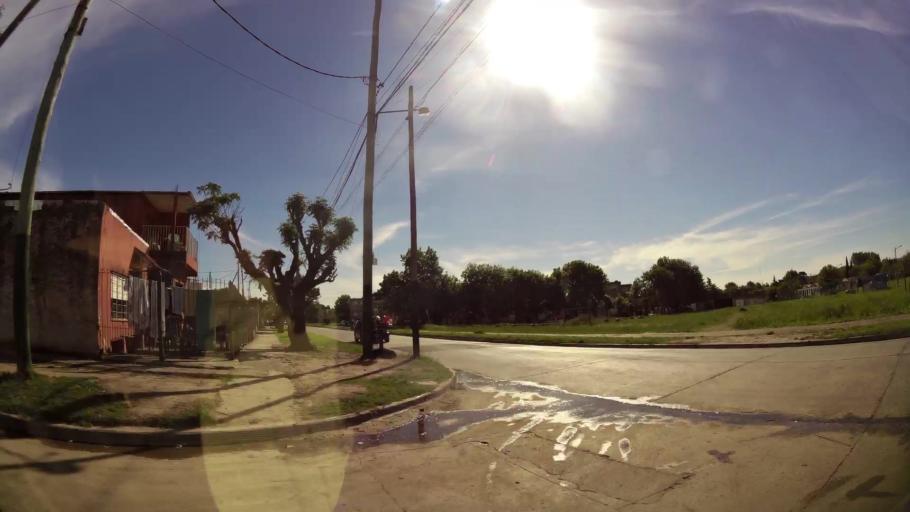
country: AR
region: Buenos Aires
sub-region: Partido de Almirante Brown
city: Adrogue
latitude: -34.8230
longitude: -58.3447
